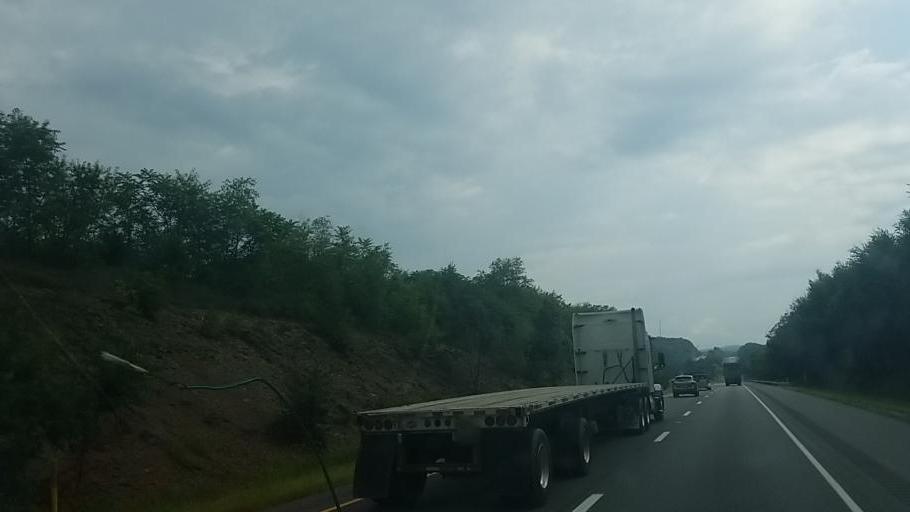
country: US
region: Pennsylvania
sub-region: Juniata County
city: Mifflintown
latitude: 40.5572
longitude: -77.2848
